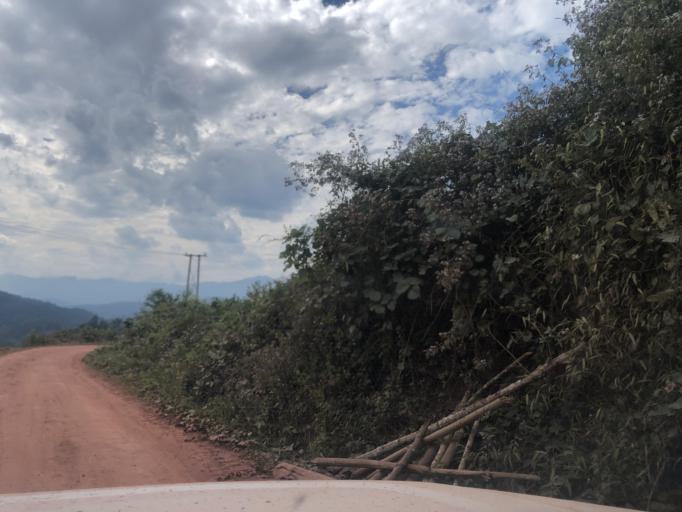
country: CN
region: Yunnan
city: Menglie
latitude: 22.1204
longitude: 101.7382
